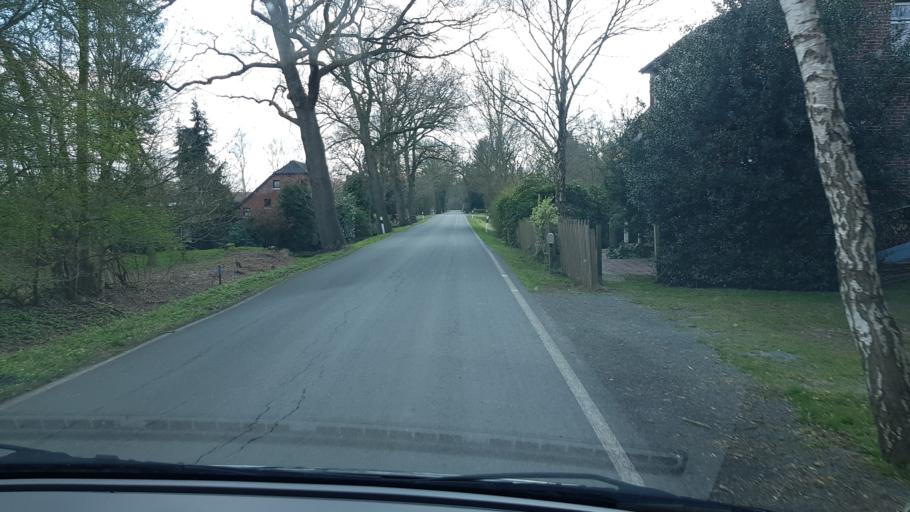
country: DE
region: Lower Saxony
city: Rastede
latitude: 53.3025
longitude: 8.2652
